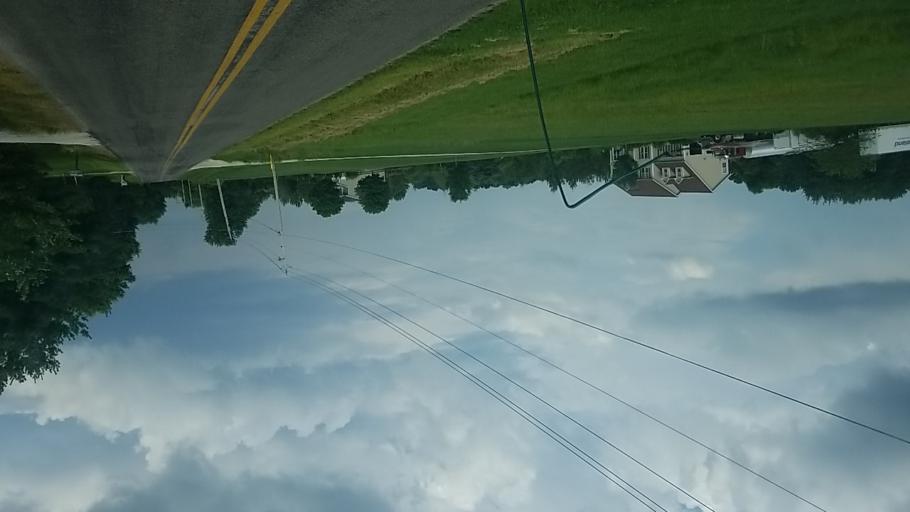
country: US
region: Ohio
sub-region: Wayne County
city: Creston
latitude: 40.9952
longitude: -81.9063
